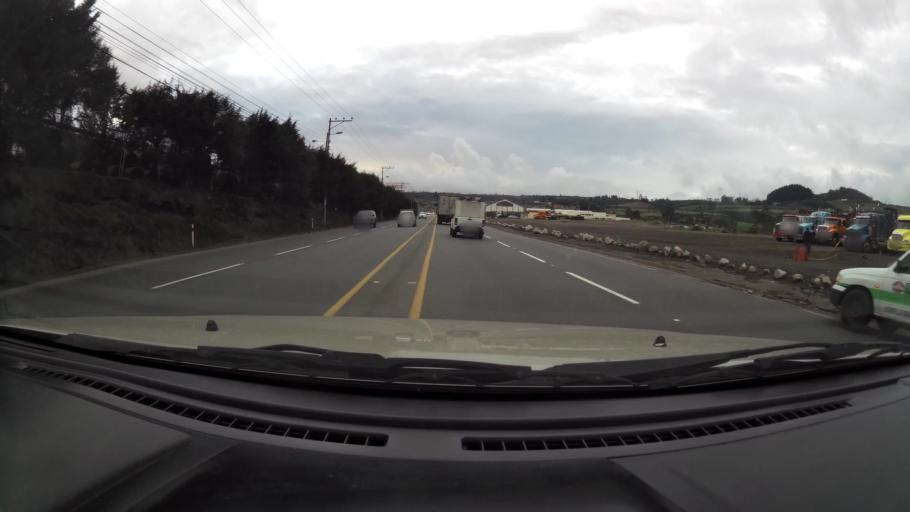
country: EC
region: Pichincha
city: Machachi
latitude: -0.4492
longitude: -78.6368
